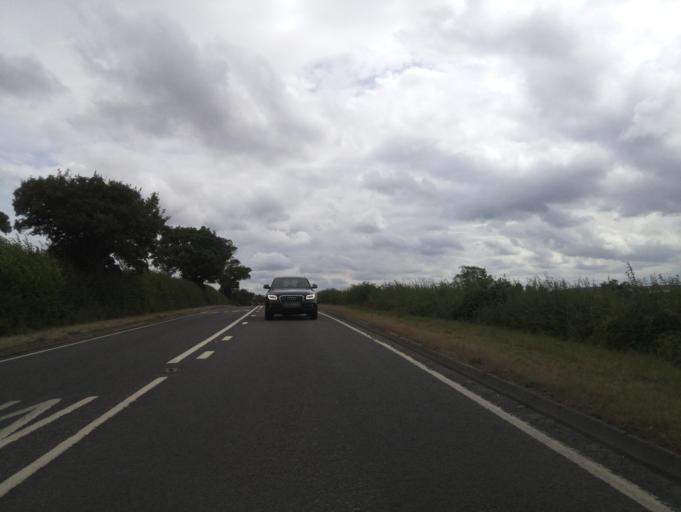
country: GB
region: England
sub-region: Leicestershire
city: Castle Donington
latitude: 52.8145
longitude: -1.3773
